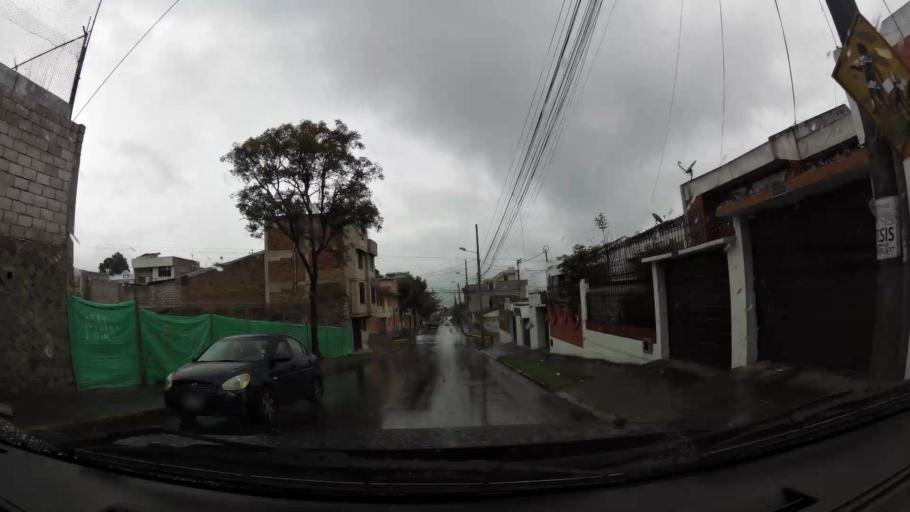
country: EC
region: Pichincha
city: Quito
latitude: -0.1188
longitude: -78.4971
